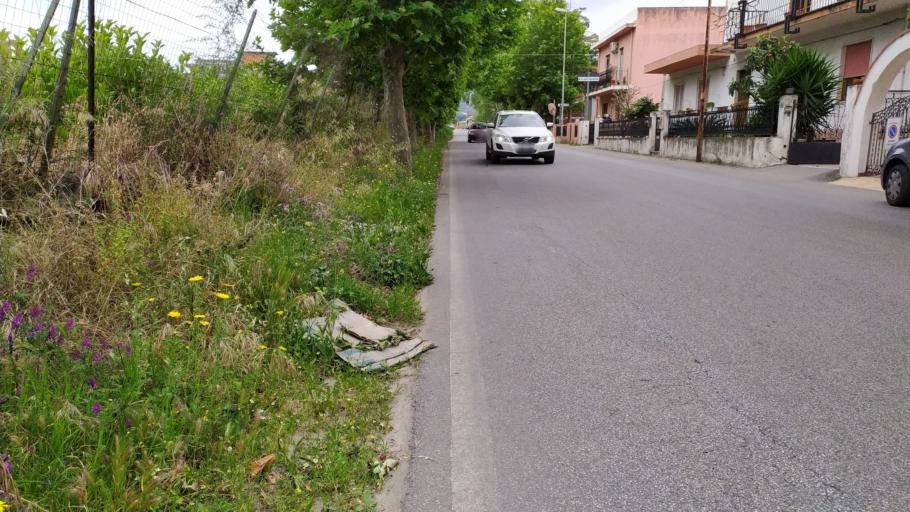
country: IT
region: Sicily
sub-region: Messina
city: Meri
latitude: 38.1866
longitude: 15.2538
